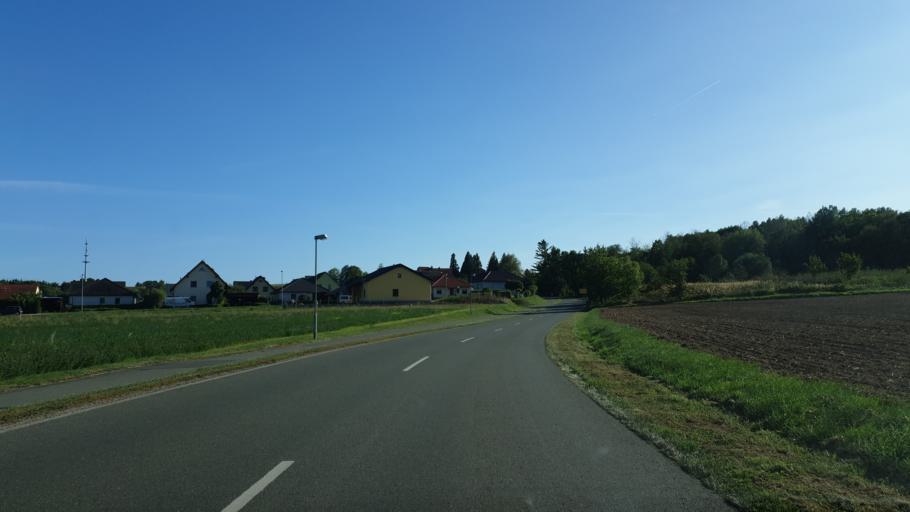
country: DE
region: Thuringia
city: Hartmannsdorf
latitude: 50.9661
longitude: 11.9772
